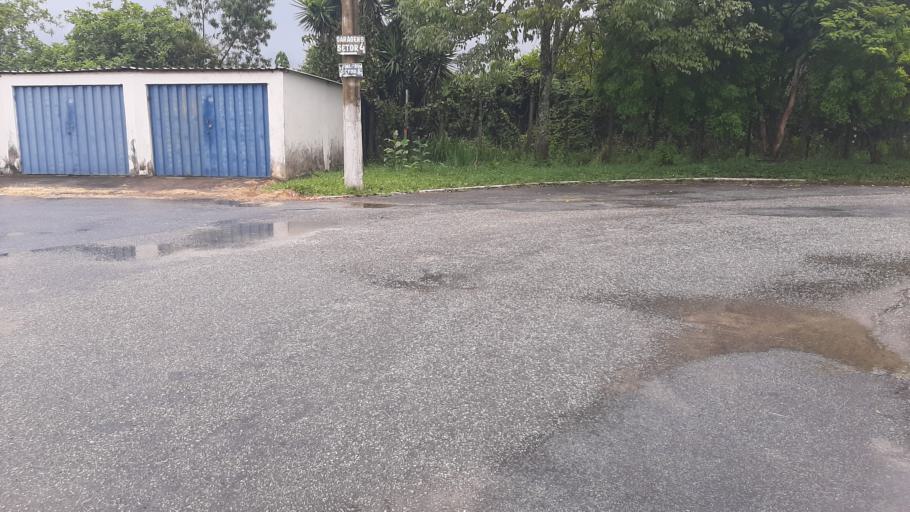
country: BR
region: Minas Gerais
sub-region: Sao Joao Del Rei
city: Sao Joao del Rei
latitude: -21.1251
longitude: -44.2352
